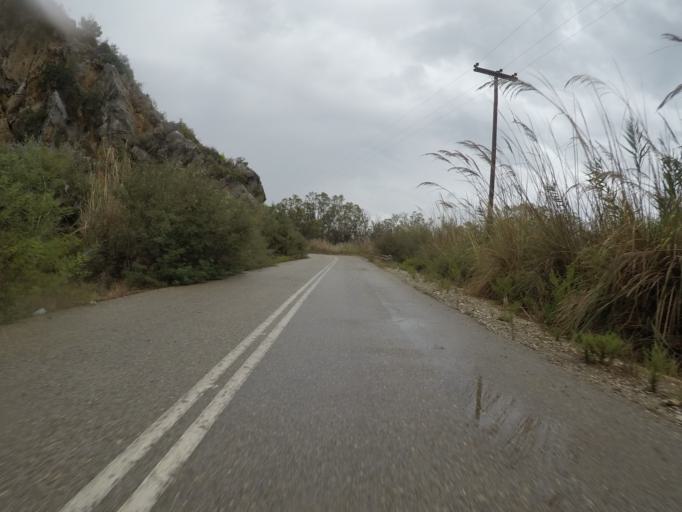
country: GR
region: West Greece
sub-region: Nomos Ileias
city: Zacharo
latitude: 37.5208
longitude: 21.6002
